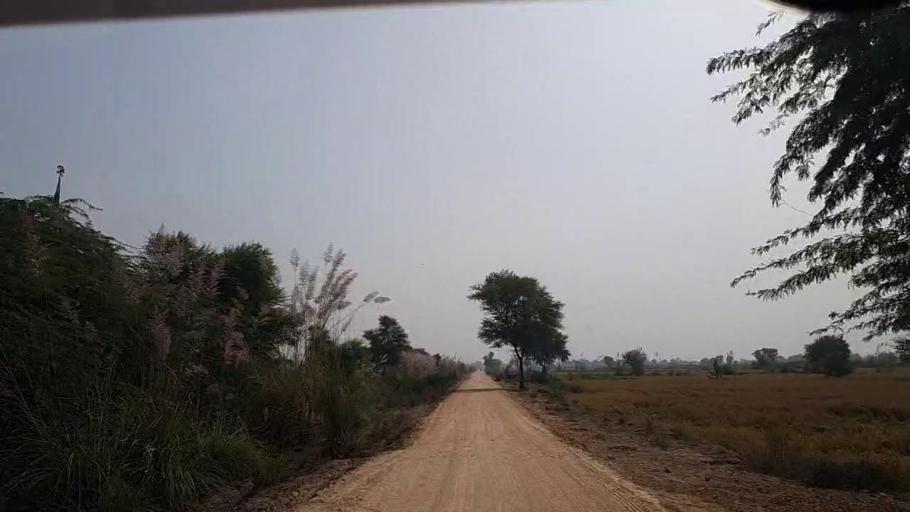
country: PK
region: Sindh
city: Garhi Yasin
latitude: 27.9298
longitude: 68.5592
